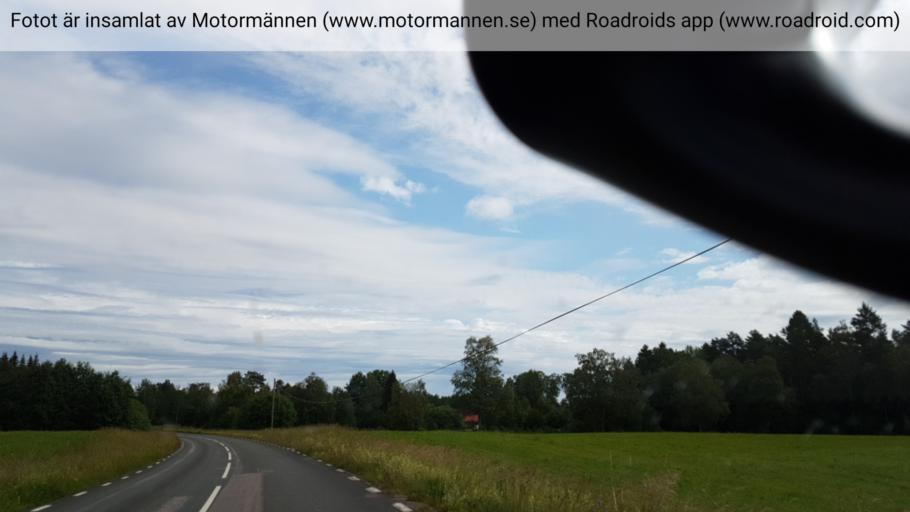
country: SE
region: Vaestra Goetaland
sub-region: Falkopings Kommun
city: Floby
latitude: 58.2021
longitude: 13.3653
